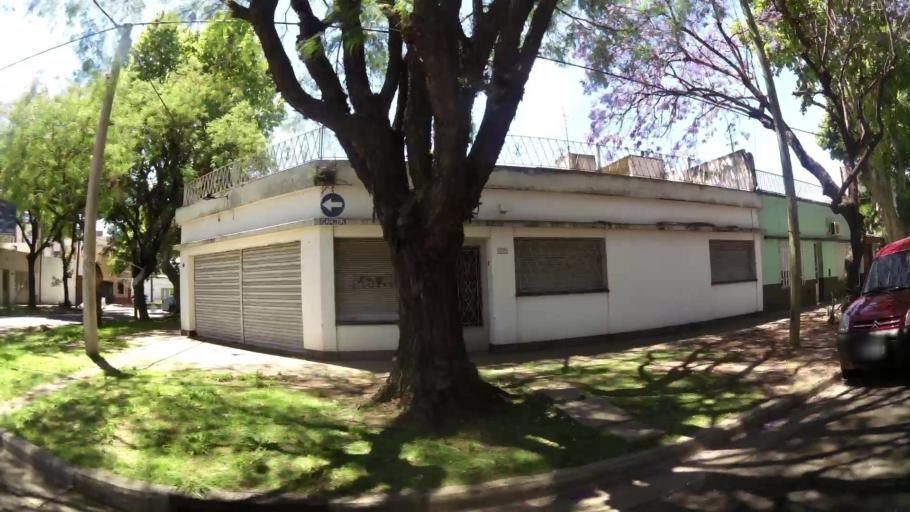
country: AR
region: Santa Fe
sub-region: Departamento de Rosario
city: Rosario
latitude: -32.9456
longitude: -60.7053
